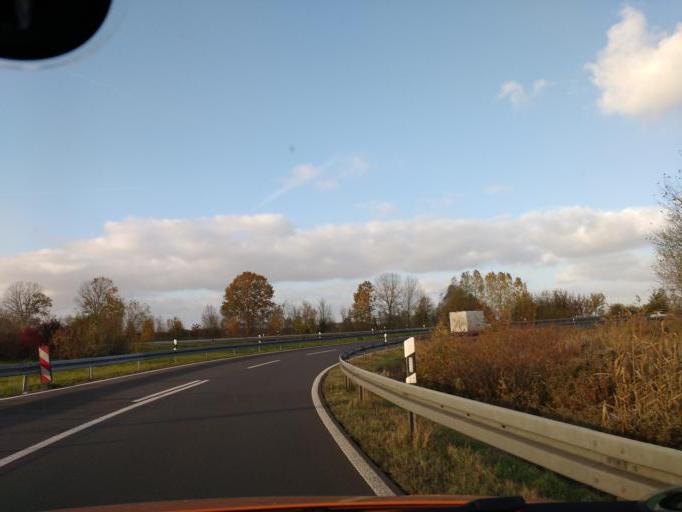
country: DE
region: Brandenburg
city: Neuenhagen
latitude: 52.5516
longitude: 13.6764
